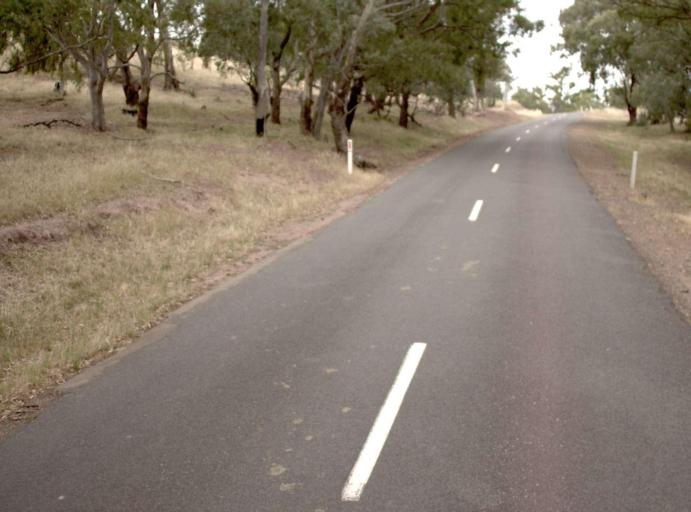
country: AU
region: Victoria
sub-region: Wellington
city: Heyfield
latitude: -37.6613
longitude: 146.6461
